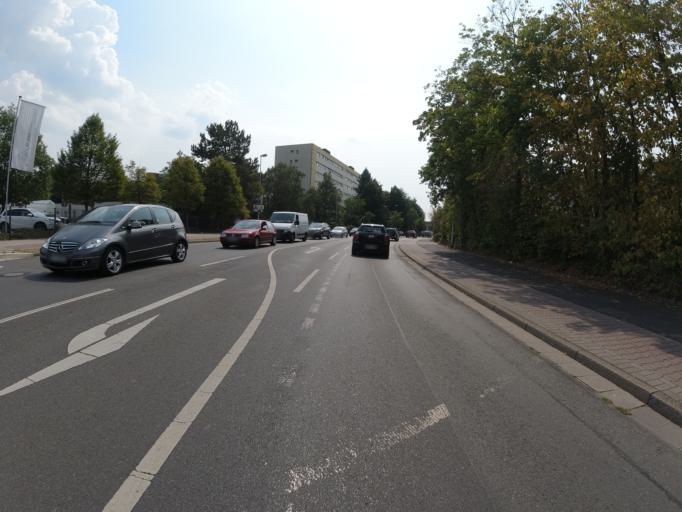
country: DE
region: North Rhine-Westphalia
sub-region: Regierungsbezirk Dusseldorf
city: Moers
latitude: 51.4456
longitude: 6.6388
